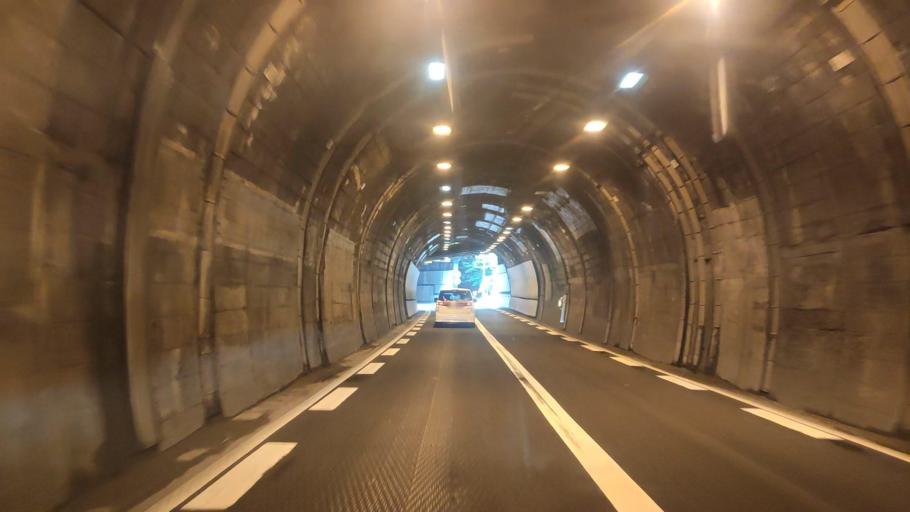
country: JP
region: Fukui
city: Takefu
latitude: 35.7851
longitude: 136.1006
